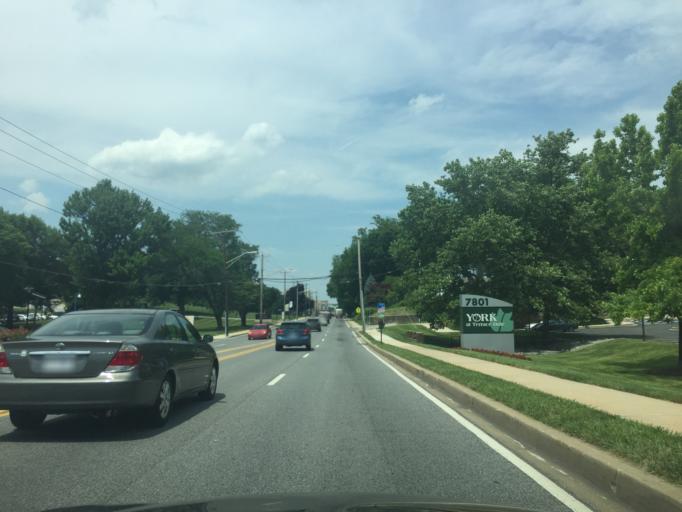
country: US
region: Maryland
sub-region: Baltimore County
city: Towson
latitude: 39.3902
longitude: -76.6052
